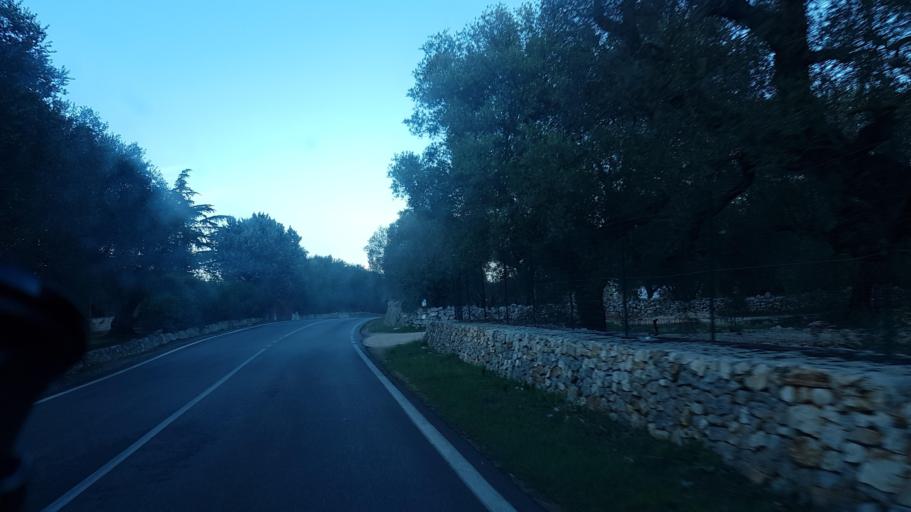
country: IT
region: Apulia
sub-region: Provincia di Brindisi
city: San Michele Salentino
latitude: 40.6577
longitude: 17.6015
